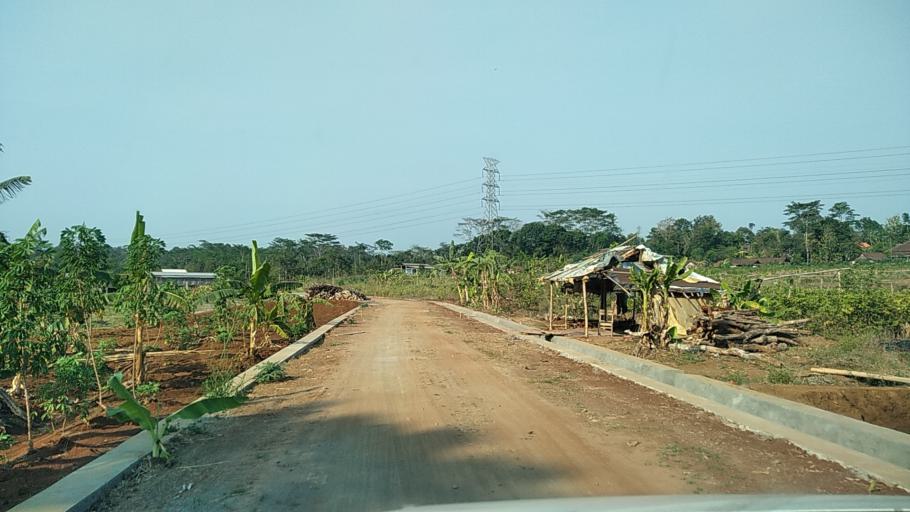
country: ID
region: Central Java
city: Ungaran
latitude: -7.0714
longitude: 110.3505
